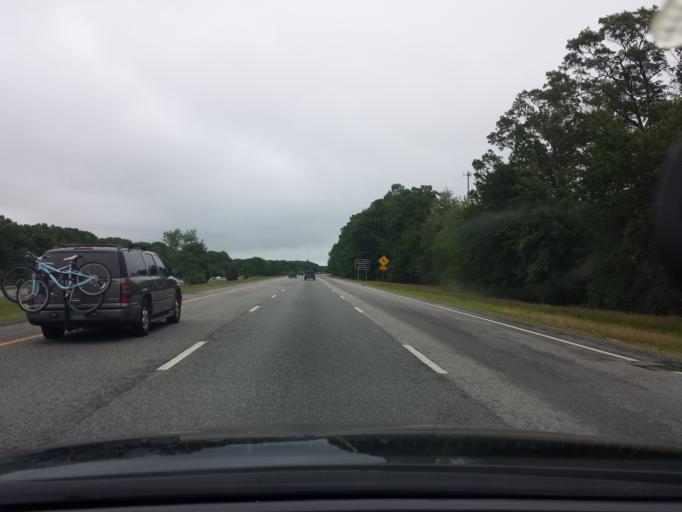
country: US
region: Rhode Island
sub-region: Washington County
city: Hope Valley
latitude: 41.5464
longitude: -71.6748
